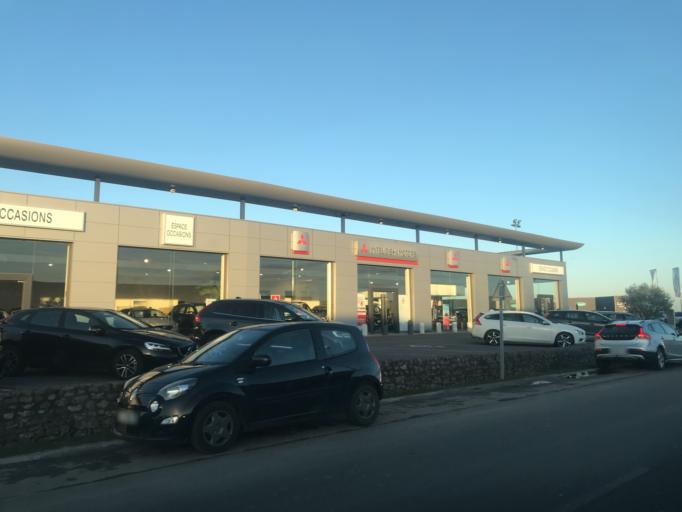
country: FR
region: Lower Normandy
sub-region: Departement du Calvados
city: Epron
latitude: 49.2273
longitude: -0.3678
